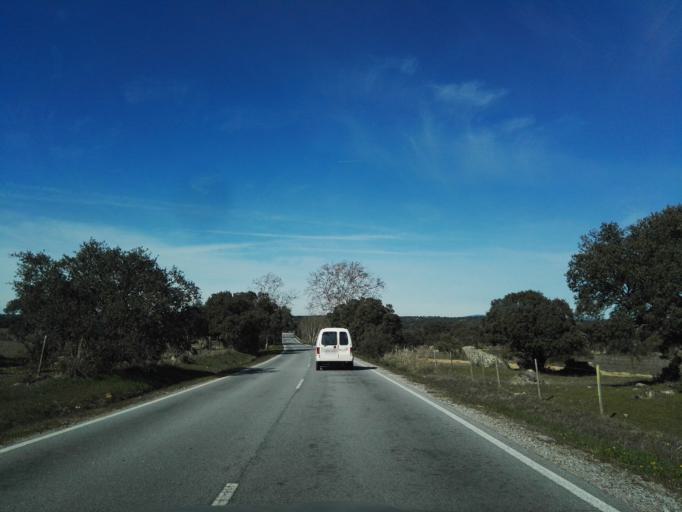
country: PT
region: Portalegre
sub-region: Arronches
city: Arronches
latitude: 39.0492
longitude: -7.2654
